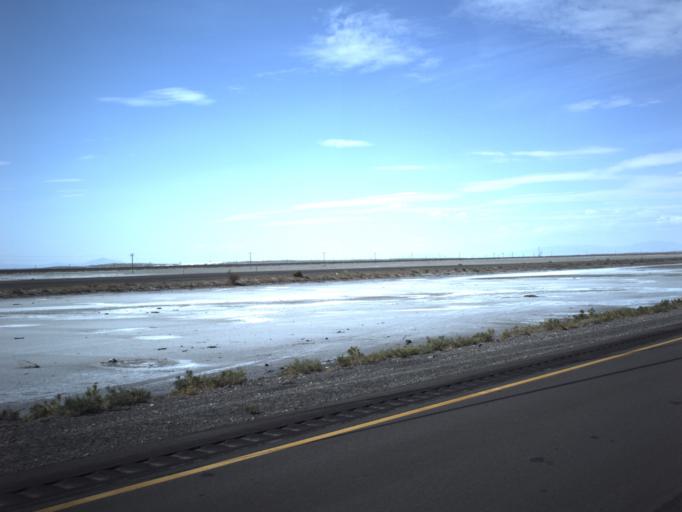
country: US
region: Utah
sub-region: Tooele County
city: Wendover
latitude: 40.7277
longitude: -113.2876
